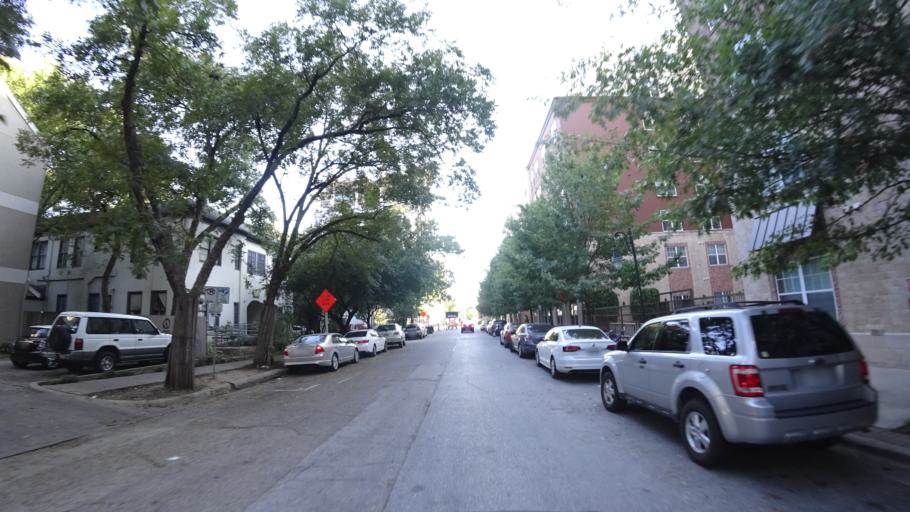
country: US
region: Texas
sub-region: Travis County
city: Austin
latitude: 30.2874
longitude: -97.7437
